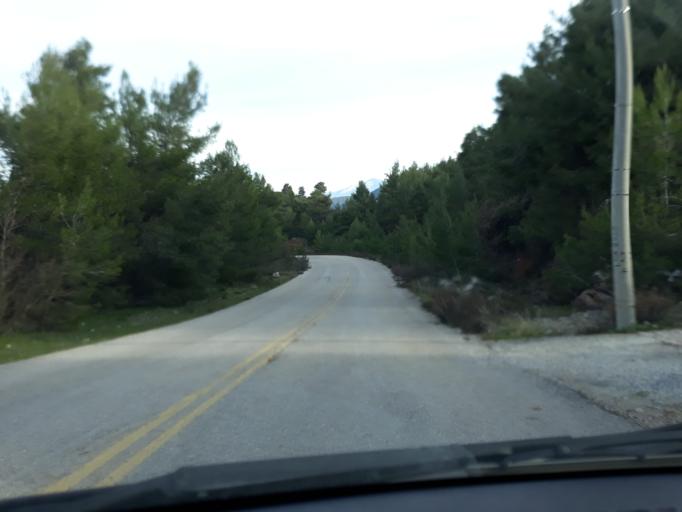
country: GR
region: Attica
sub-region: Nomarchia Anatolikis Attikis
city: Afidnes
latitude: 38.2120
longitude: 23.7980
